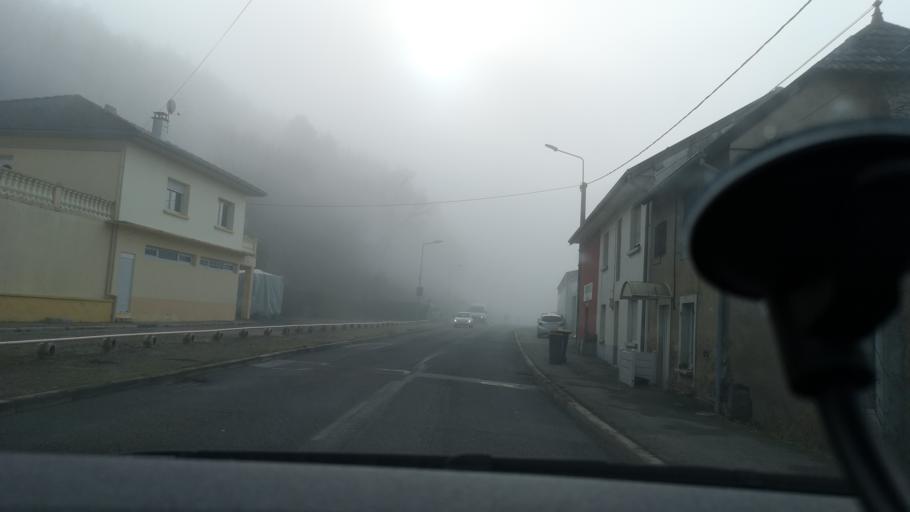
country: FR
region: Franche-Comte
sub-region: Departement du Doubs
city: Clerval
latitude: 47.4227
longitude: 6.5626
